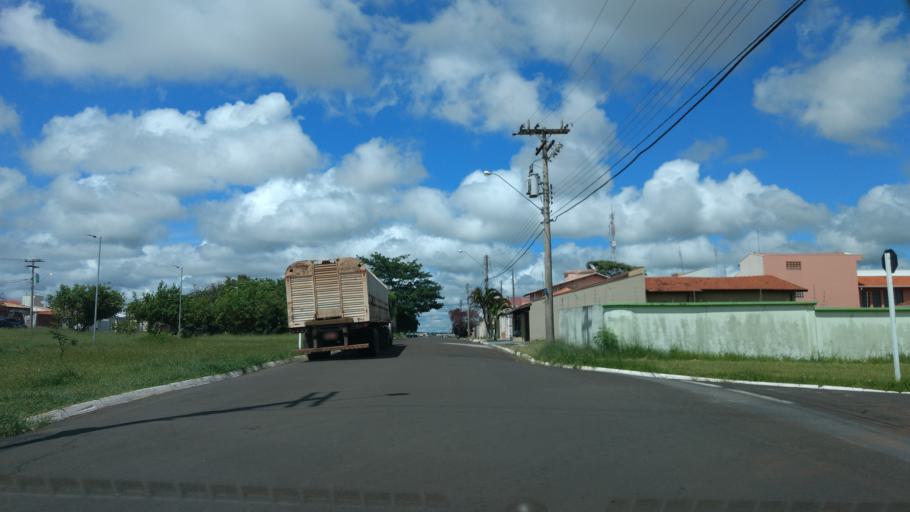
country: BR
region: Sao Paulo
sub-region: Botucatu
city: Botucatu
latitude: -22.8532
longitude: -48.4405
